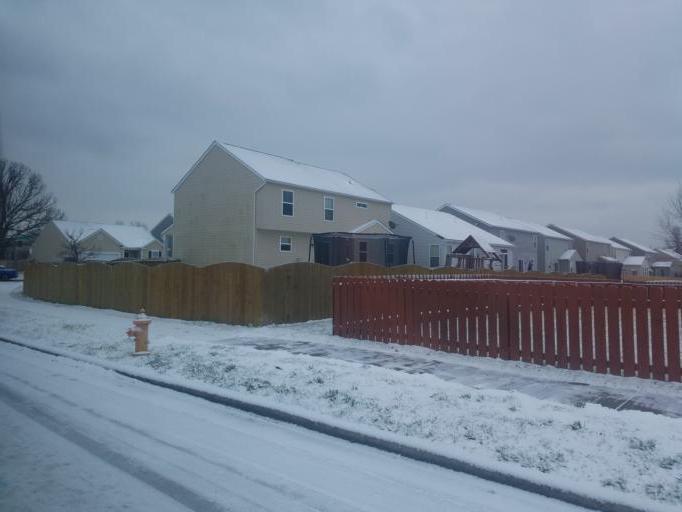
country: US
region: Ohio
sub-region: Franklin County
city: Reynoldsburg
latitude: 39.9977
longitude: -82.7974
